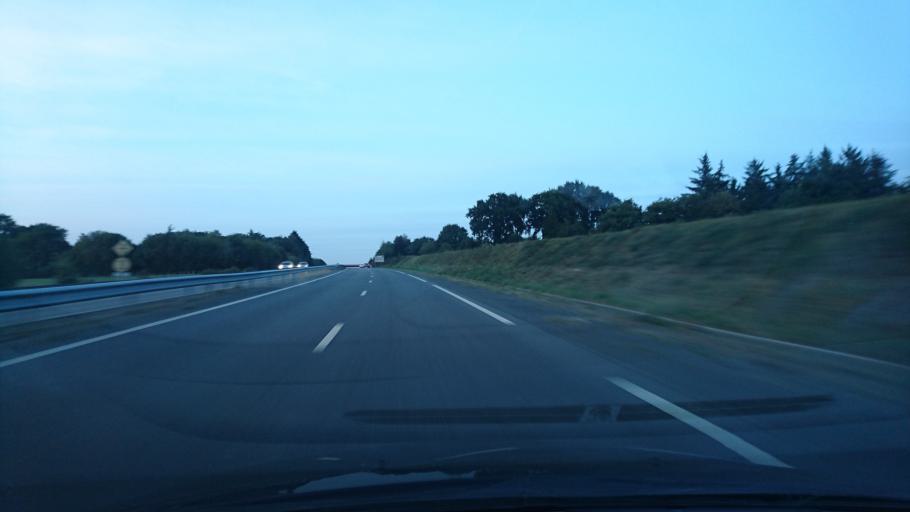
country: FR
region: Brittany
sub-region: Departement d'Ille-et-Vilaine
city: Guichen
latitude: 47.9561
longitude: -1.8162
